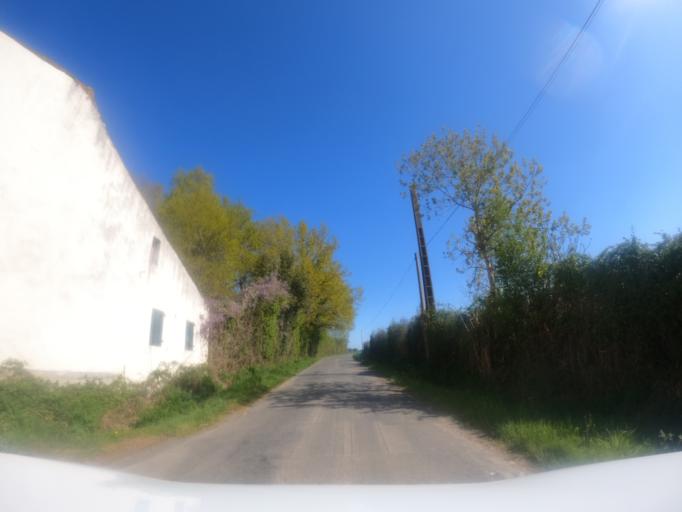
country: FR
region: Pays de la Loire
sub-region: Departement de la Vendee
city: Le Champ-Saint-Pere
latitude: 46.5365
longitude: -1.3508
